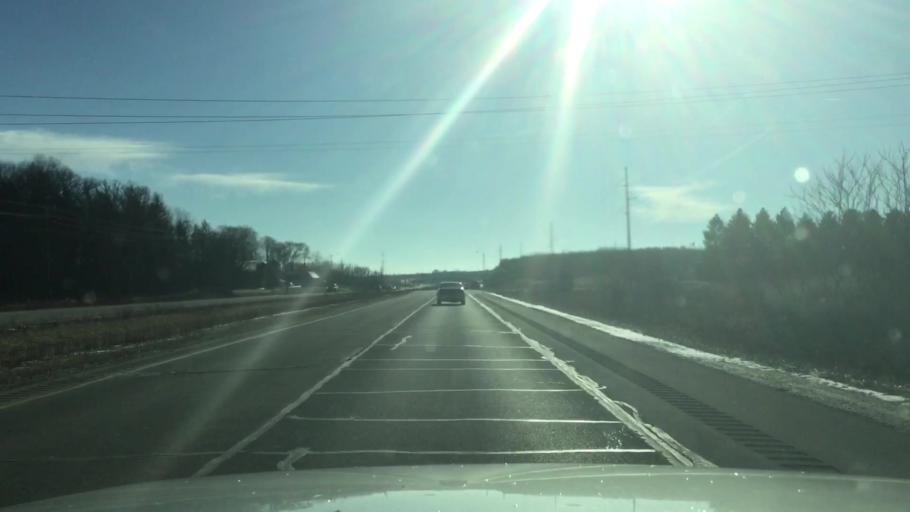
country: US
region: Wisconsin
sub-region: Racine County
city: Rochester
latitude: 42.7286
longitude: -88.2211
